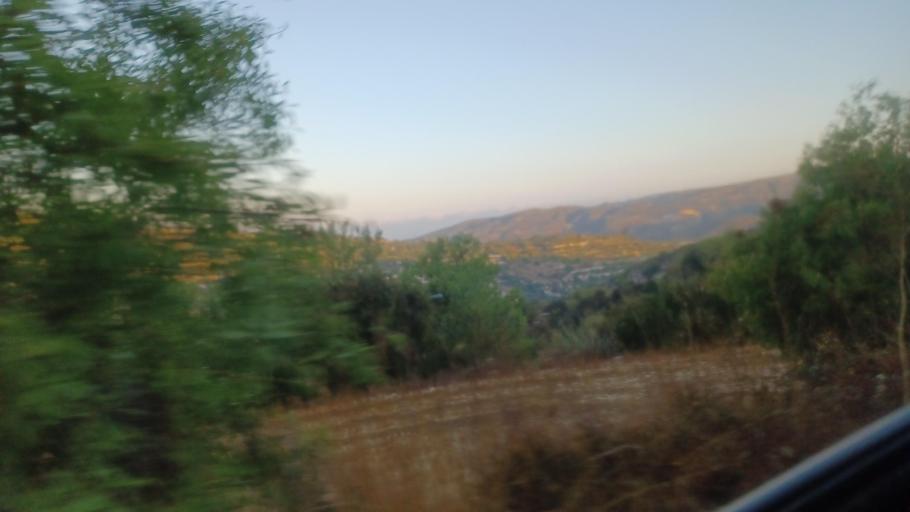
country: CY
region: Pafos
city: Tala
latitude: 34.8599
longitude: 32.4688
